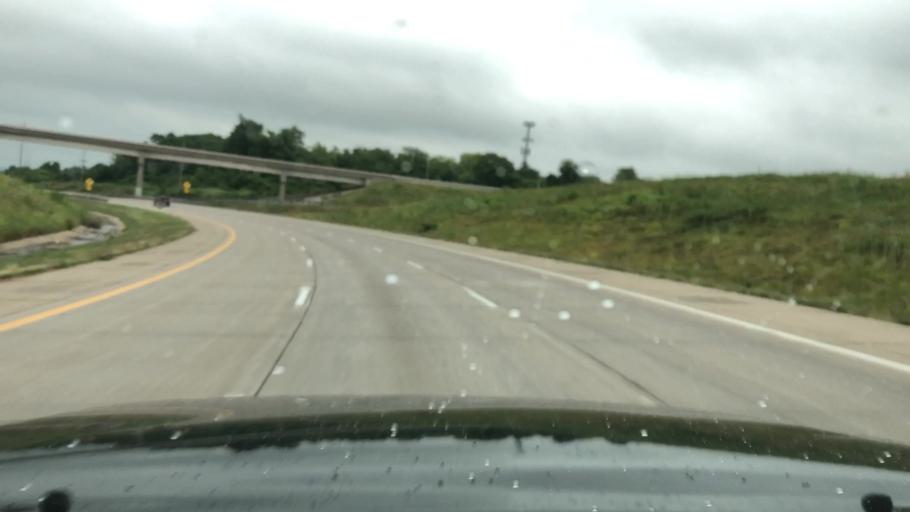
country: US
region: Missouri
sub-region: Saint Charles County
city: Saint Peters
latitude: 38.7992
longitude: -90.5906
